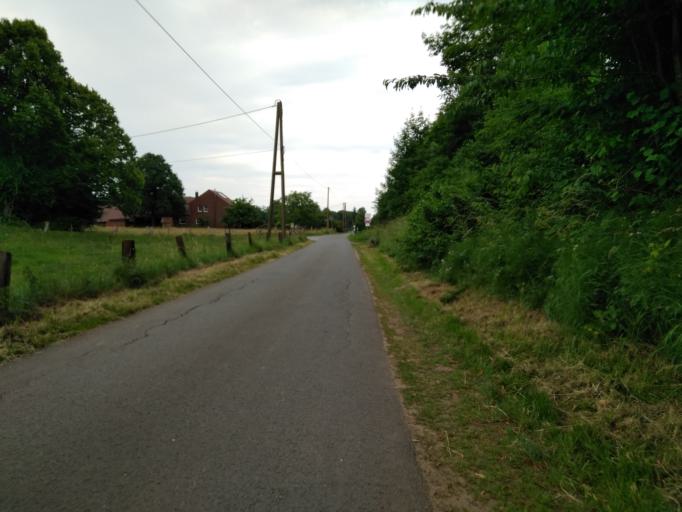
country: DE
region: North Rhine-Westphalia
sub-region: Regierungsbezirk Dusseldorf
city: Schermbeck
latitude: 51.6663
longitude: 6.8920
